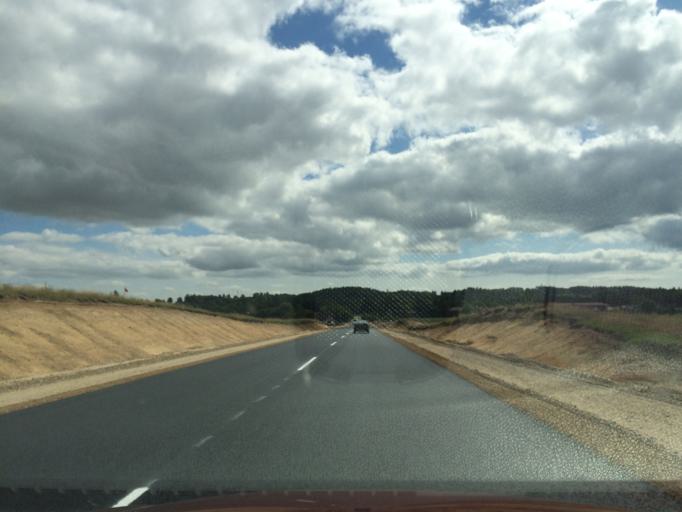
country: DK
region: Central Jutland
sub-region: Silkeborg Kommune
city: Svejbaek
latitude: 56.1849
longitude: 9.6359
